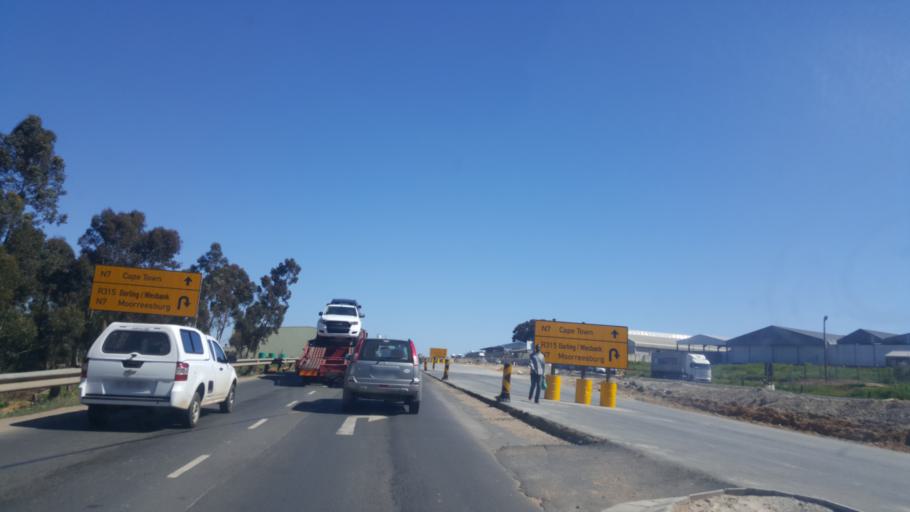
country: ZA
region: Western Cape
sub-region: West Coast District Municipality
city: Malmesbury
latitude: -33.4674
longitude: 18.7160
